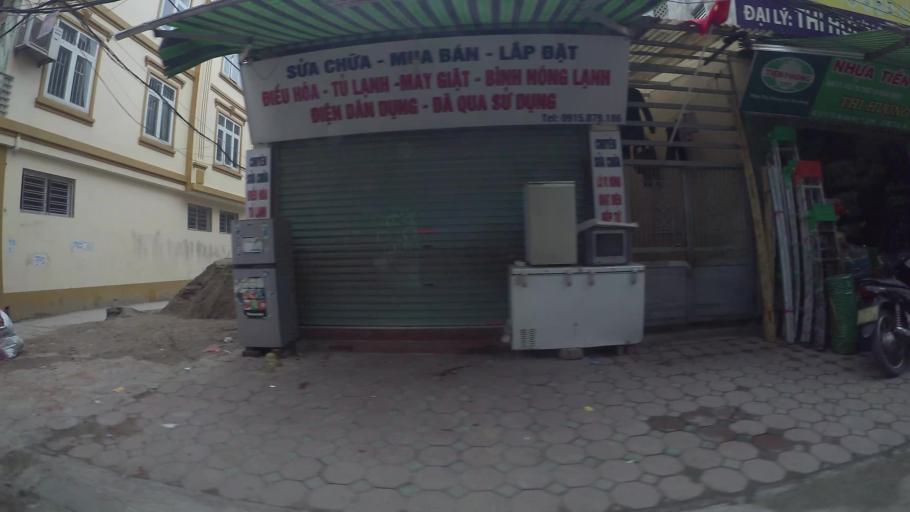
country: VN
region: Ha Noi
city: Hai BaTrung
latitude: 20.9915
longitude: 105.8589
